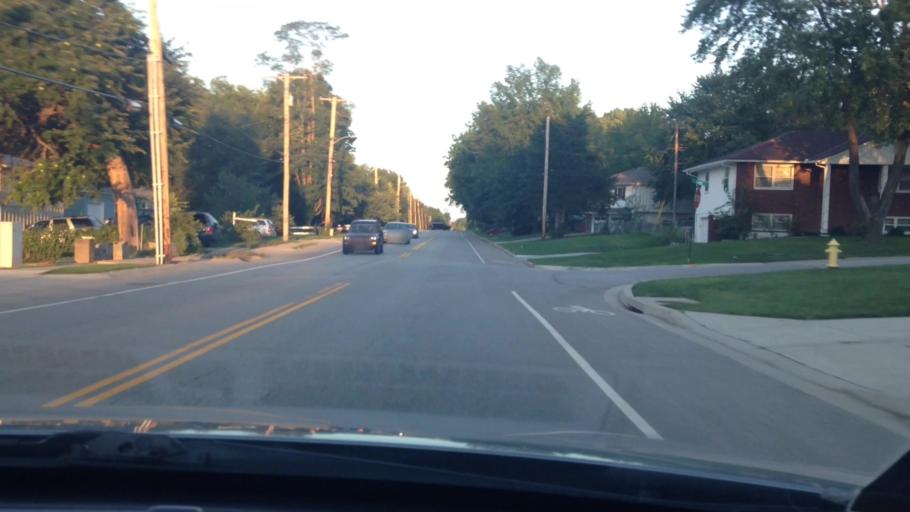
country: US
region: Missouri
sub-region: Jackson County
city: Raytown
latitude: 38.9731
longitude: -94.4795
